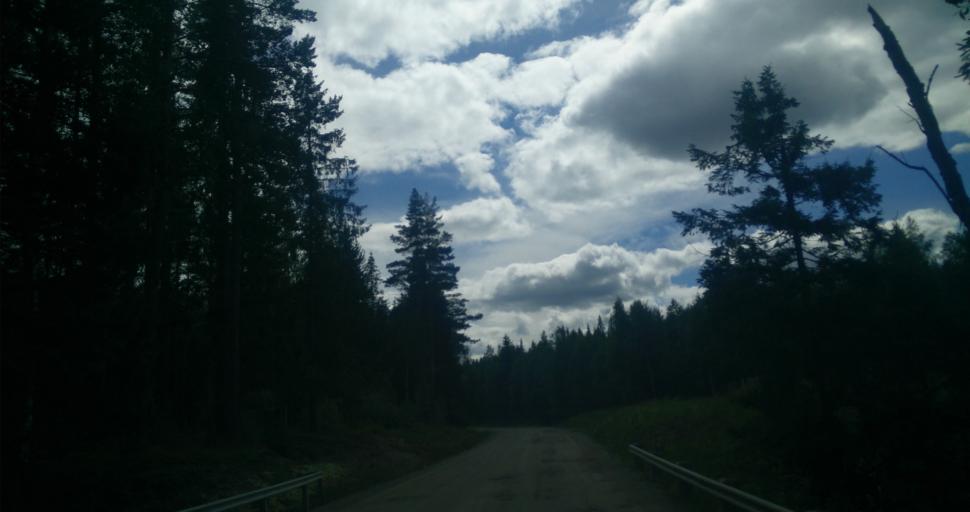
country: SE
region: Gaevleborg
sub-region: Nordanstigs Kommun
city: Bergsjoe
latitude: 62.1102
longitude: 17.0993
